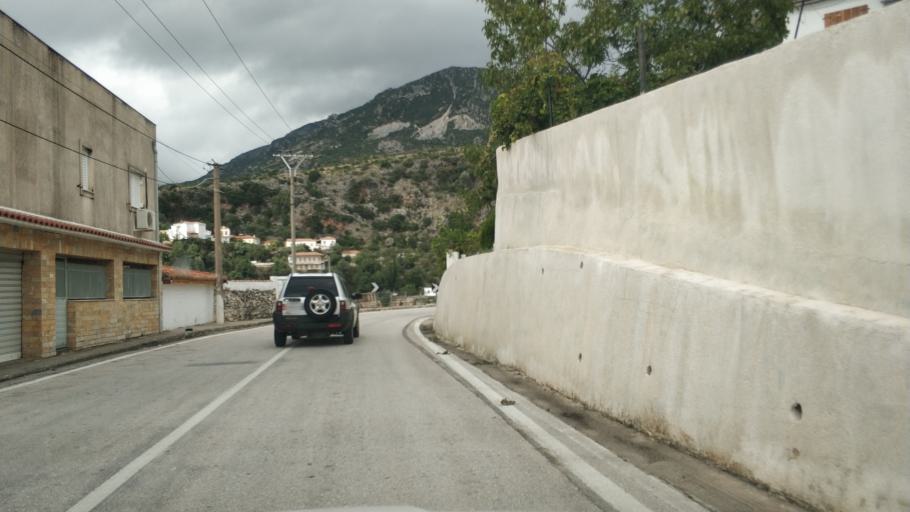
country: AL
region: Vlore
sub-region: Rrethi i Vlores
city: Vranisht
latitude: 40.1518
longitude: 19.6386
